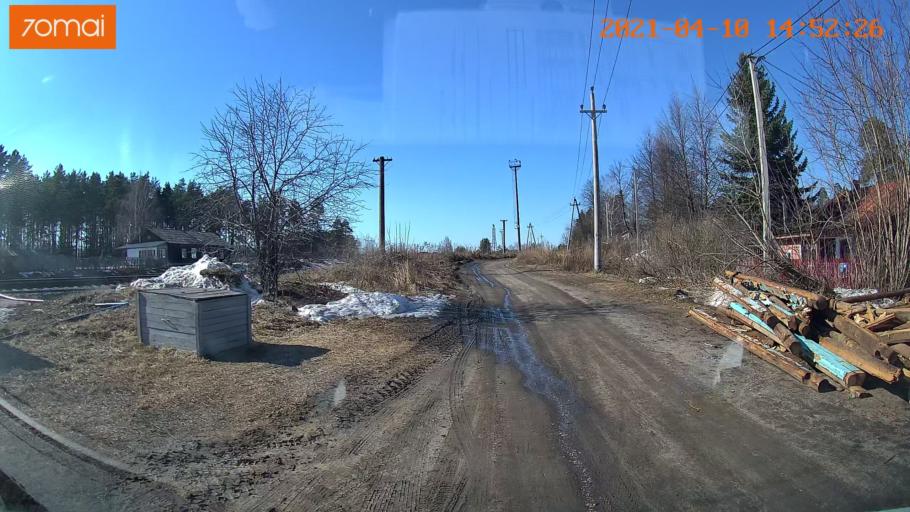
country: RU
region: Ivanovo
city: Kokhma
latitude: 56.9853
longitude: 41.0615
